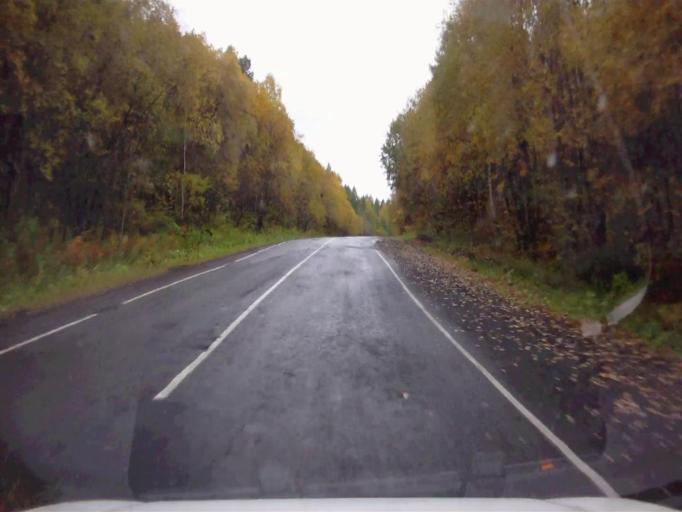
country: RU
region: Chelyabinsk
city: Verkhniy Ufaley
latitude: 56.0441
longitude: 60.1082
